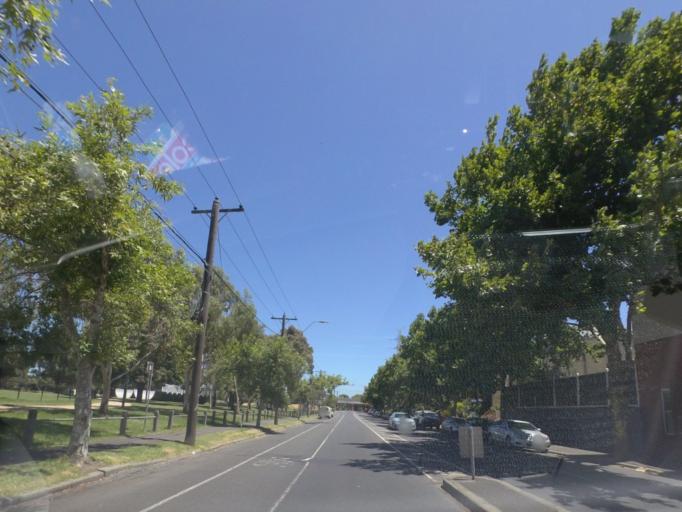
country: AU
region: Victoria
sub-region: Moonee Valley
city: Flemington
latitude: -37.7974
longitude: 144.9220
